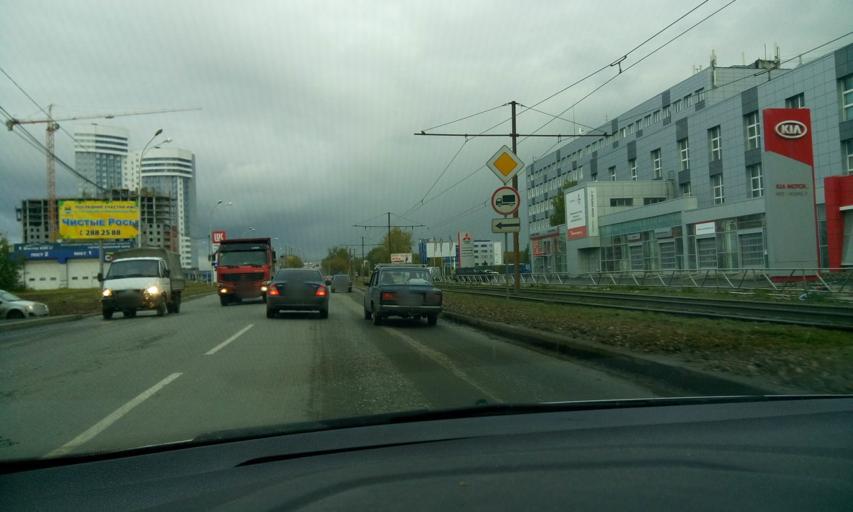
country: RU
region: Sverdlovsk
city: Yekaterinburg
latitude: 56.8624
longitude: 60.6643
